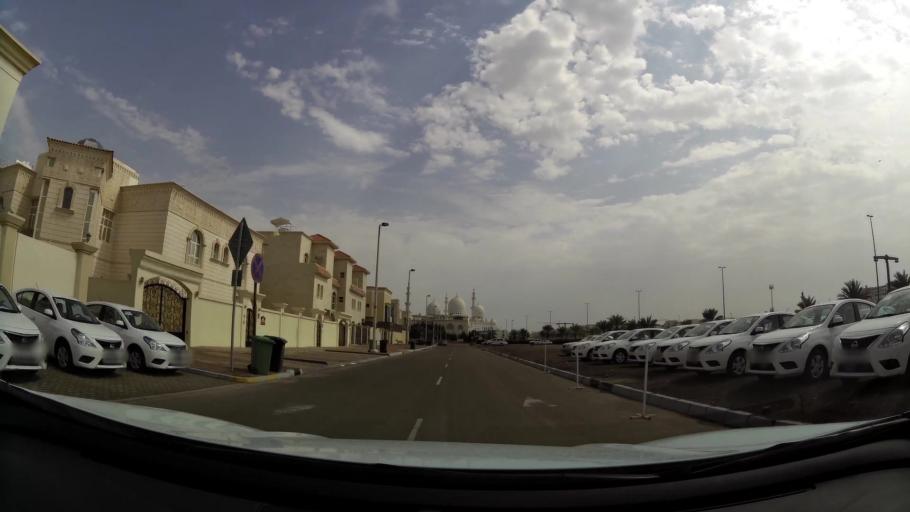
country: AE
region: Abu Dhabi
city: Abu Dhabi
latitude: 24.4144
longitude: 54.4664
